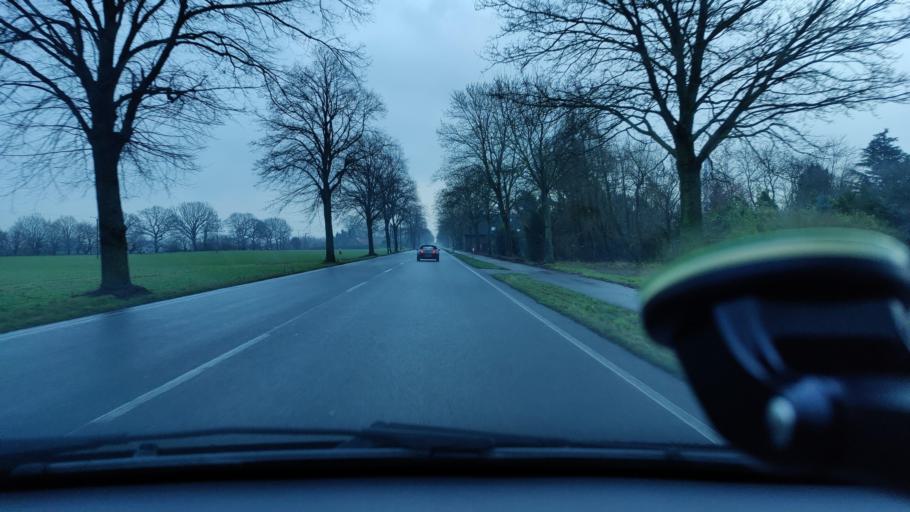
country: DE
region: North Rhine-Westphalia
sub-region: Regierungsbezirk Dusseldorf
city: Alpen
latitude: 51.5864
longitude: 6.5469
